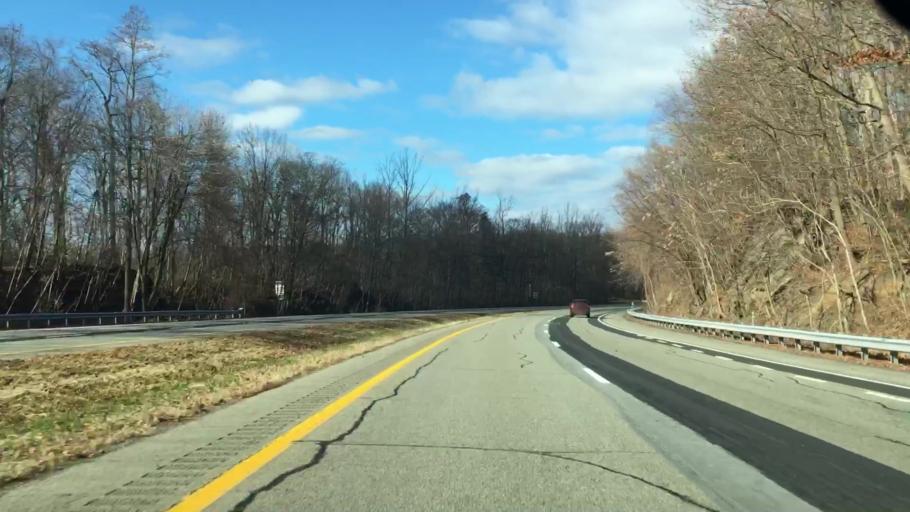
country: US
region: New York
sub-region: Westchester County
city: Purchase
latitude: 41.0258
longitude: -73.7232
